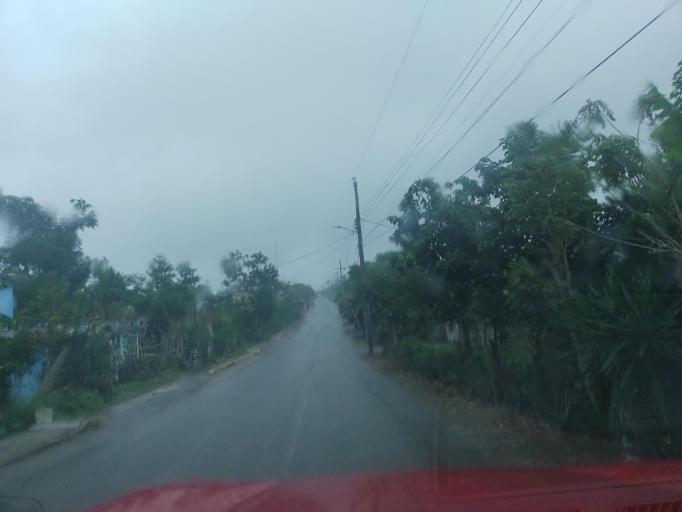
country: MX
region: Veracruz
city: Agua Dulce
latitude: 20.3367
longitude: -97.3165
